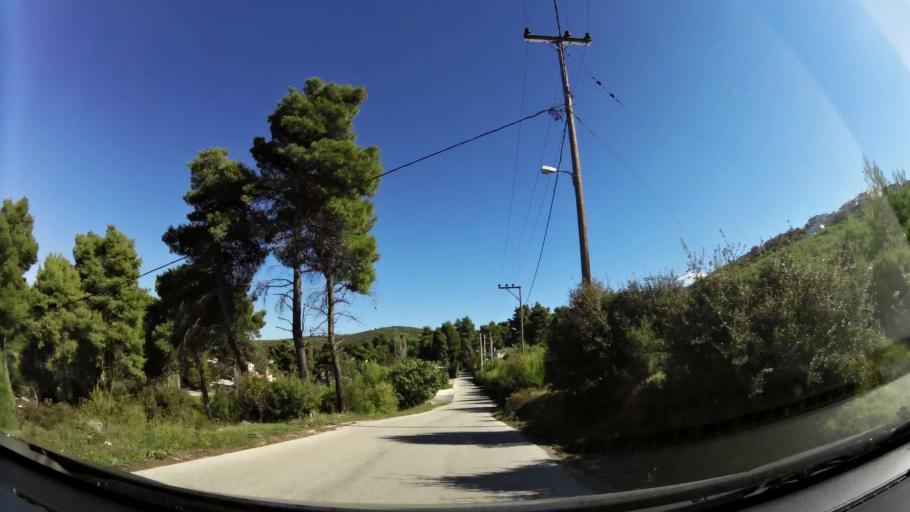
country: GR
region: Attica
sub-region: Nomarchia Anatolikis Attikis
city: Rodopoli
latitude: 38.1152
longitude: 23.8814
